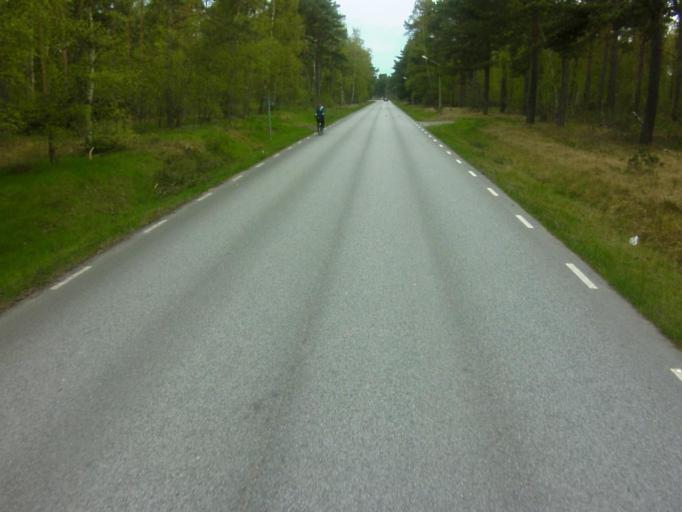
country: SE
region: Skane
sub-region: Kavlinge Kommun
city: Loddekopinge
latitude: 55.7563
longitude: 12.9939
